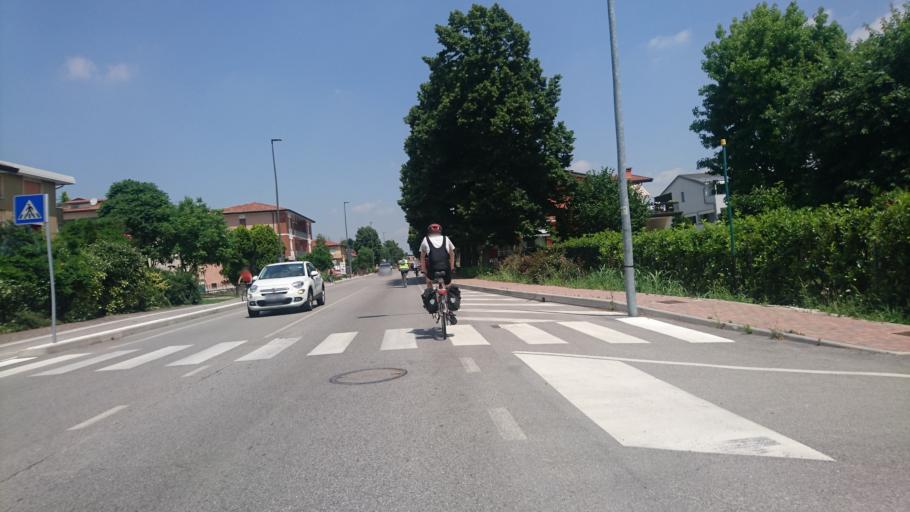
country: IT
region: Veneto
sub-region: Provincia di Venezia
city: Fiesso
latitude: 45.4150
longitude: 12.0525
